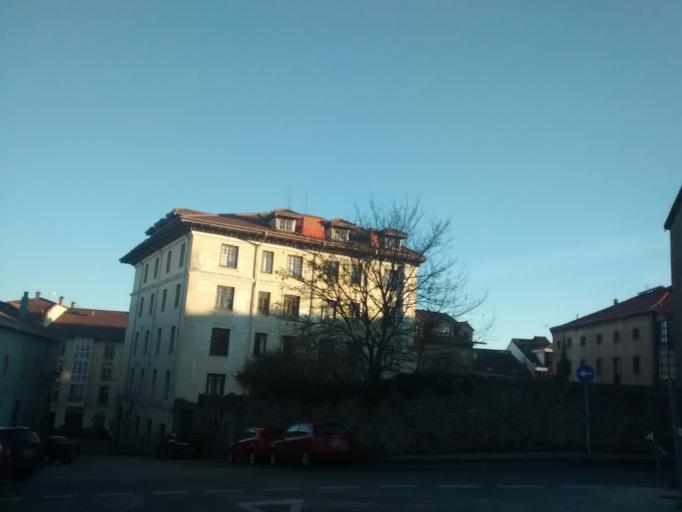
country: ES
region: Cantabria
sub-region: Provincia de Cantabria
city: Reinosa
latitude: 43.0022
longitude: -4.1371
